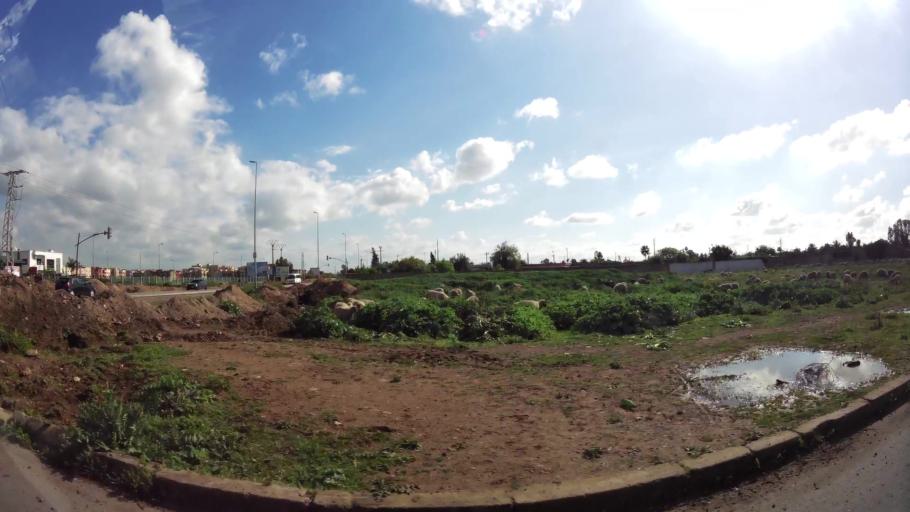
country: MA
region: Grand Casablanca
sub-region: Mediouna
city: Mediouna
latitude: 33.3880
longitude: -7.5372
